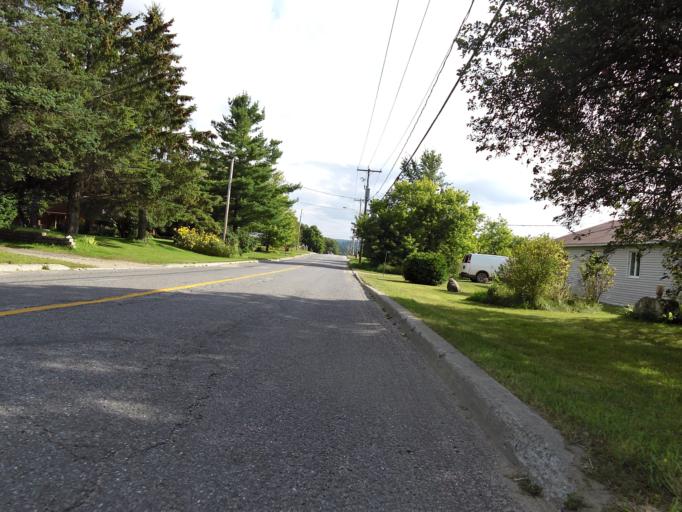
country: CA
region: Quebec
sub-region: Outaouais
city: Wakefield
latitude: 45.6483
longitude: -76.0154
